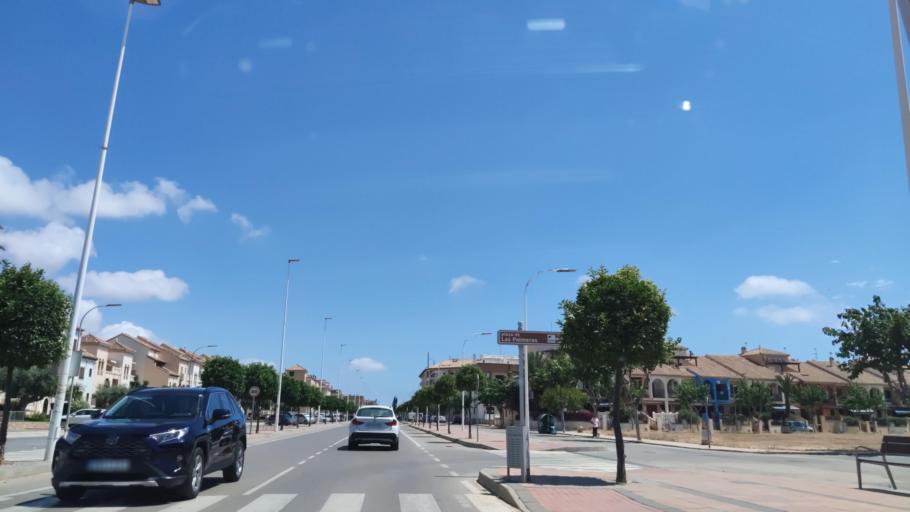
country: ES
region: Murcia
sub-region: Murcia
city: Los Alcazares
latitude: 37.7525
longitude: -0.8437
